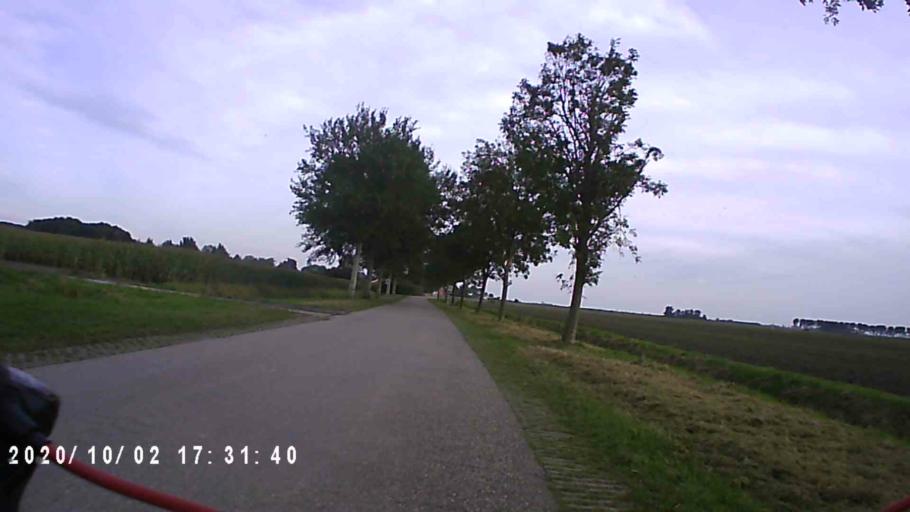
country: NL
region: Groningen
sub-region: Gemeente De Marne
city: Ulrum
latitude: 53.3362
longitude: 6.3333
